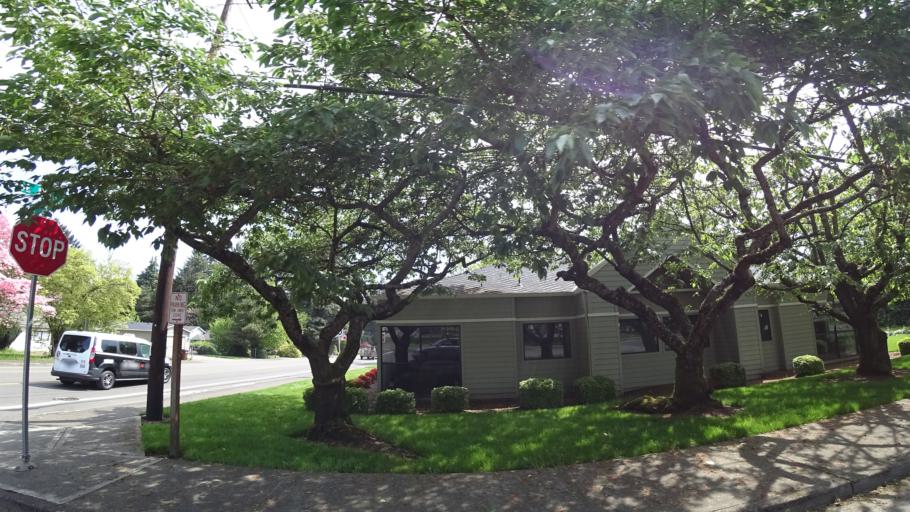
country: US
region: Oregon
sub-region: Clackamas County
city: Milwaukie
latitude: 45.4479
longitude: -122.6169
